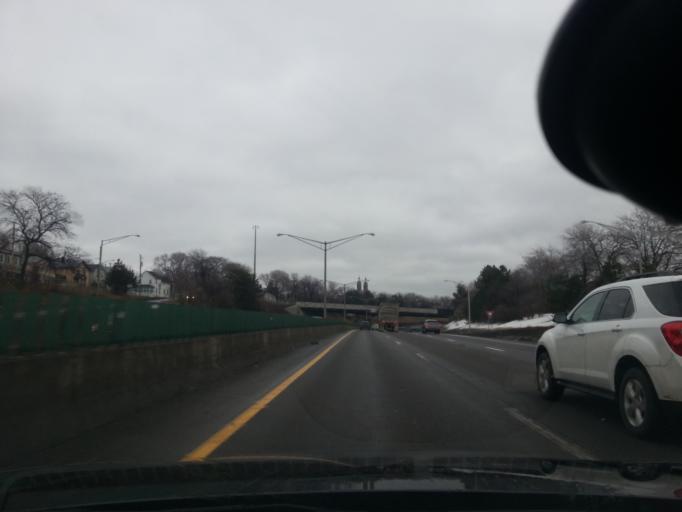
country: US
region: New York
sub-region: Onondaga County
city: Syracuse
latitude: 43.0658
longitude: -76.1626
